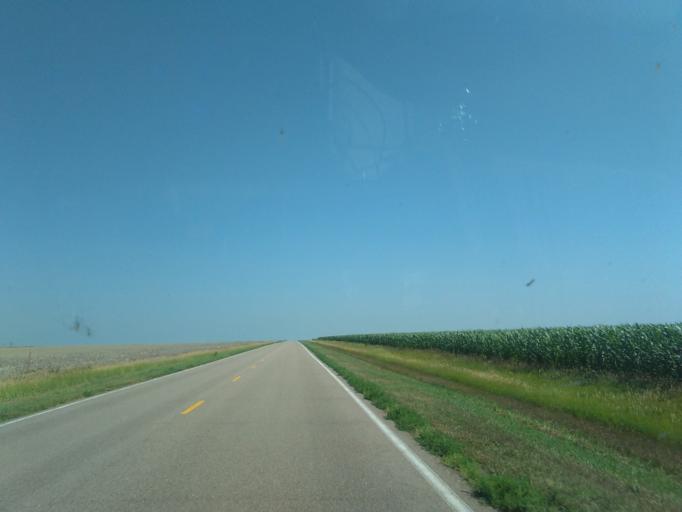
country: US
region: Nebraska
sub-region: Dundy County
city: Benkelman
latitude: 39.9190
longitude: -101.5412
